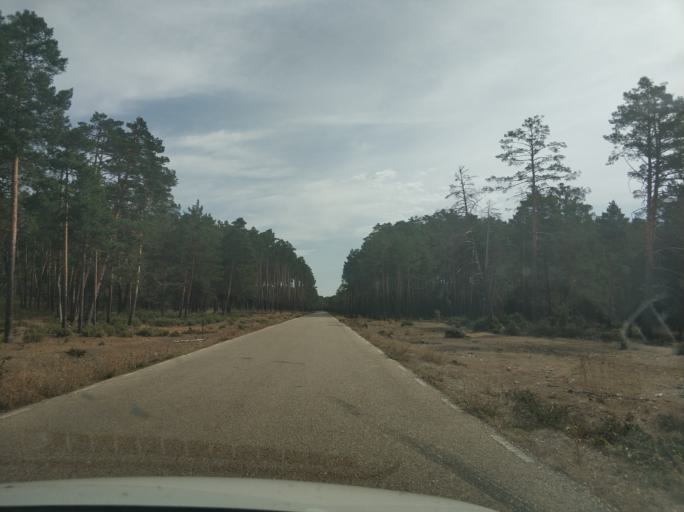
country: ES
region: Castille and Leon
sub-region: Provincia de Soria
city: Navaleno
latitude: 41.8546
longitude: -2.9542
